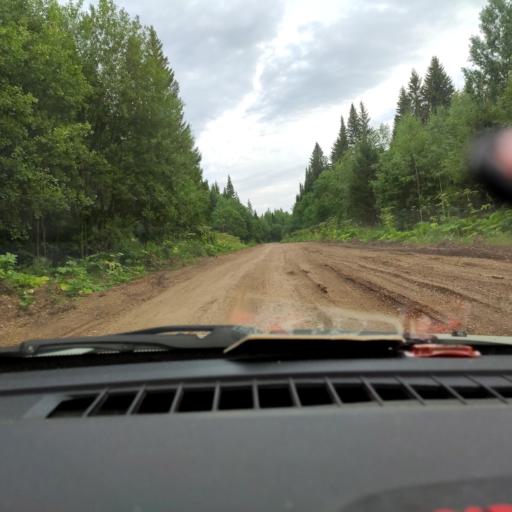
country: RU
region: Perm
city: Kultayevo
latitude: 57.8135
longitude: 56.0022
